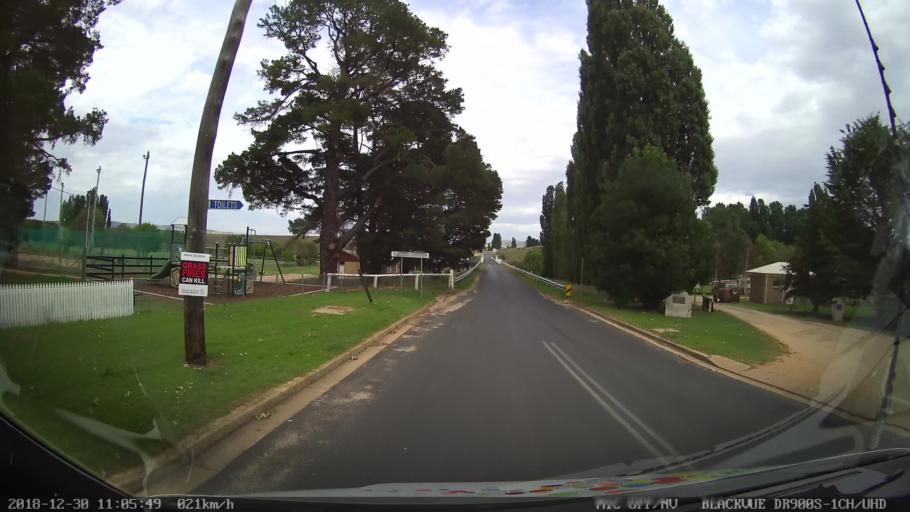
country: AU
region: New South Wales
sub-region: Snowy River
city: Berridale
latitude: -36.5042
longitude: 148.8338
